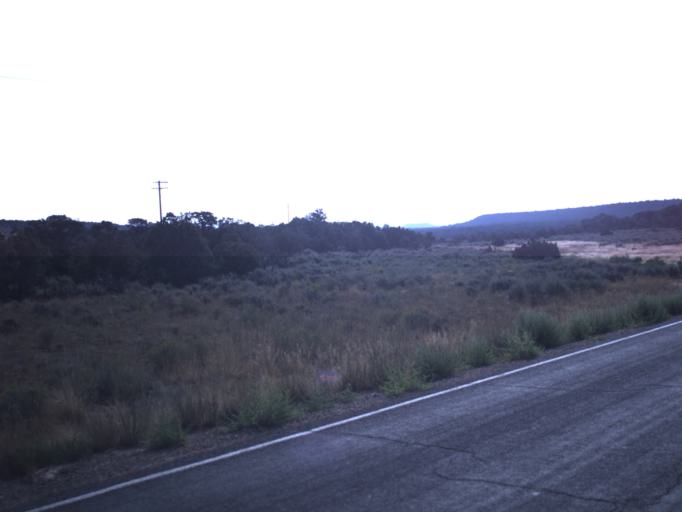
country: US
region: Utah
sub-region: Duchesne County
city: Duchesne
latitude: 40.3192
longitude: -110.3950
